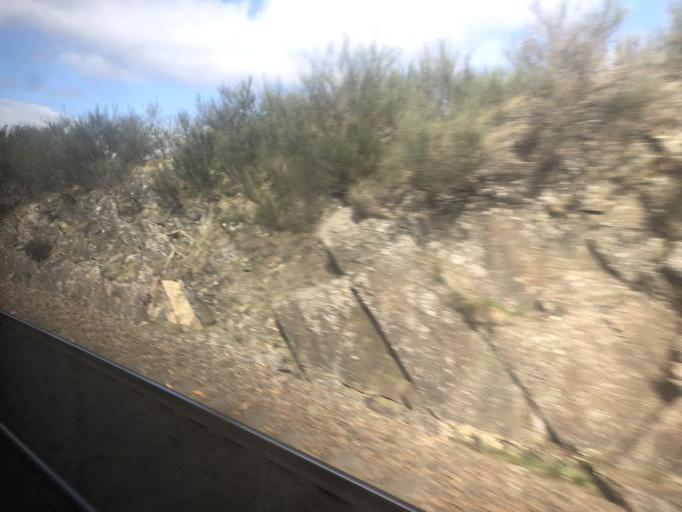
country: GB
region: Scotland
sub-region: Perth and Kinross
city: Aberfeldy
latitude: 56.7919
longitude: -4.0181
